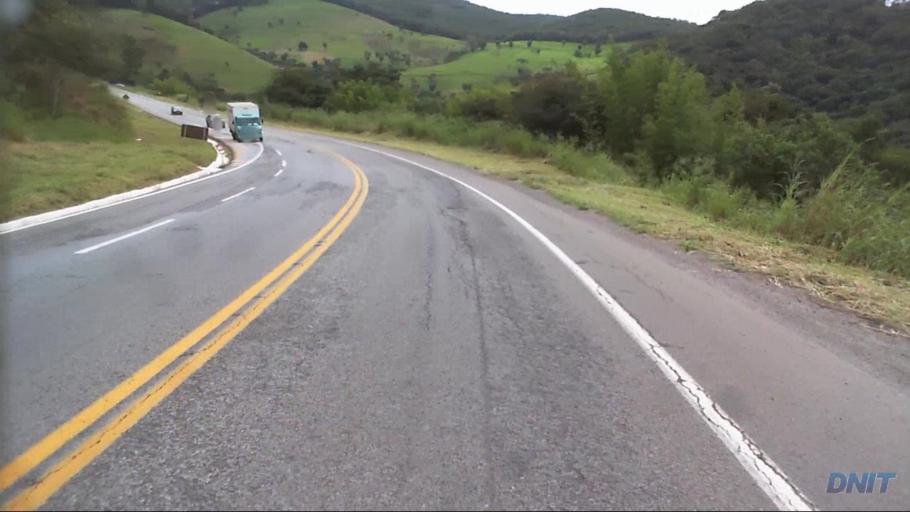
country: BR
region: Minas Gerais
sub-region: Joao Monlevade
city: Joao Monlevade
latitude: -19.8483
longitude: -43.2489
